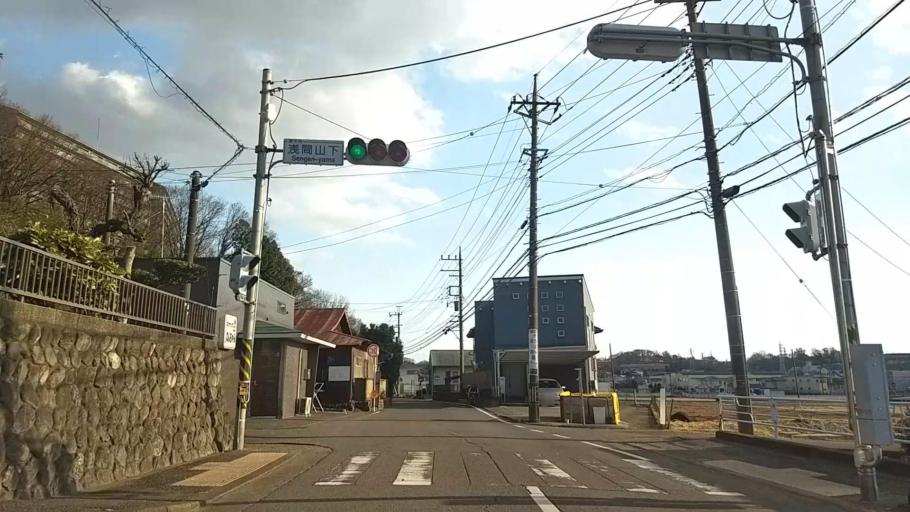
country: JP
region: Kanagawa
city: Atsugi
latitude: 35.4435
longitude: 139.3378
